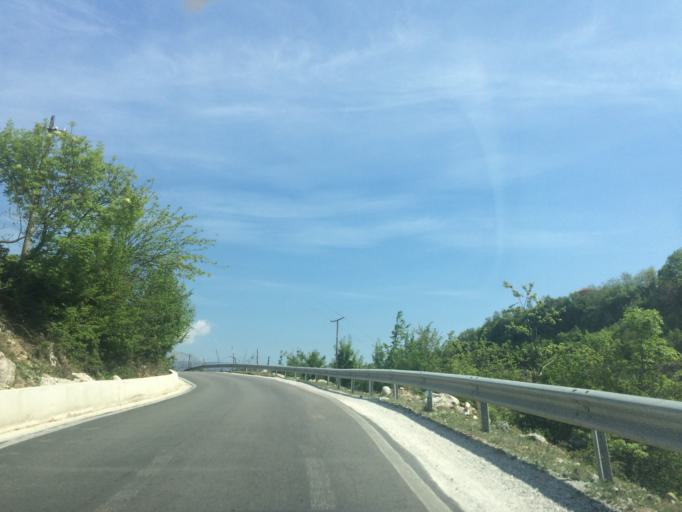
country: AL
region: Kukes
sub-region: Rrethi i Tropojes
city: Llugaj
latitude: 42.3549
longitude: 20.0966
